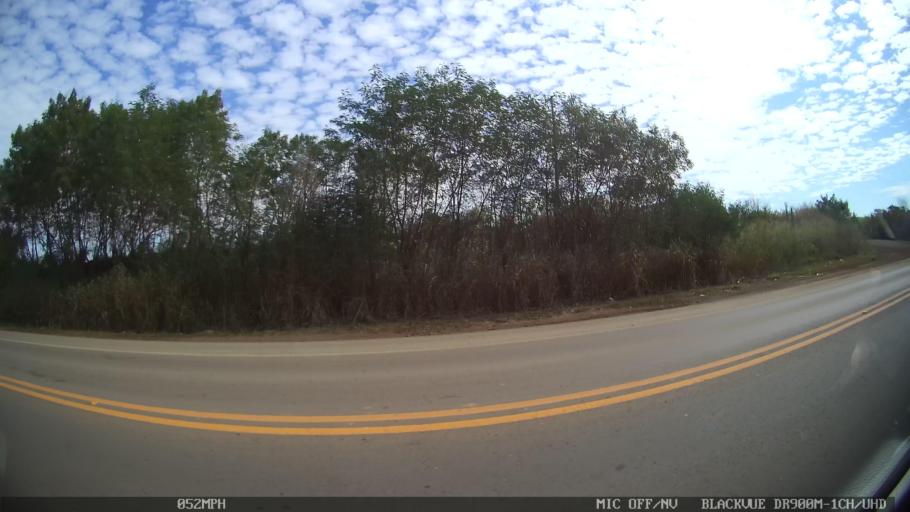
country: BR
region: Sao Paulo
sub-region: Santa Barbara D'Oeste
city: Santa Barbara d'Oeste
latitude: -22.7279
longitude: -47.4252
